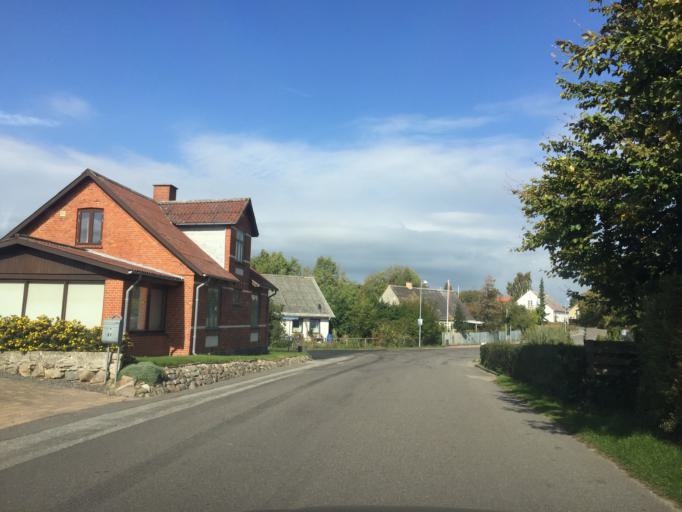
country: DK
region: Zealand
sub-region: Guldborgsund Kommune
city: Stubbekobing
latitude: 54.9235
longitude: 12.0473
